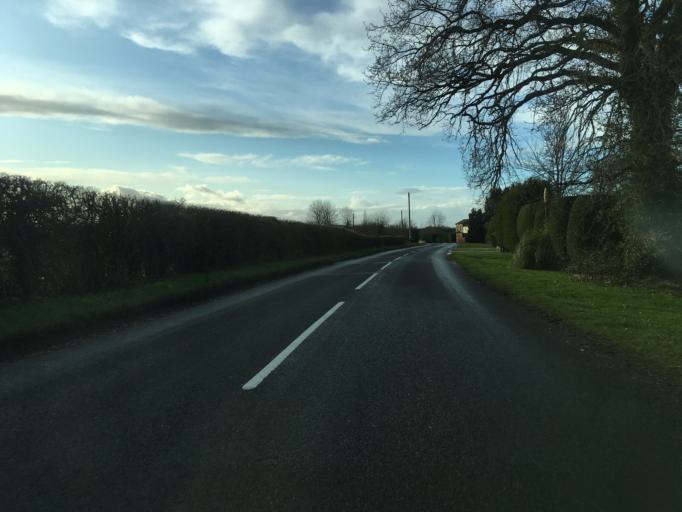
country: GB
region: England
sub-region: Warwickshire
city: Stratford-upon-Avon
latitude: 52.2249
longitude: -1.7408
